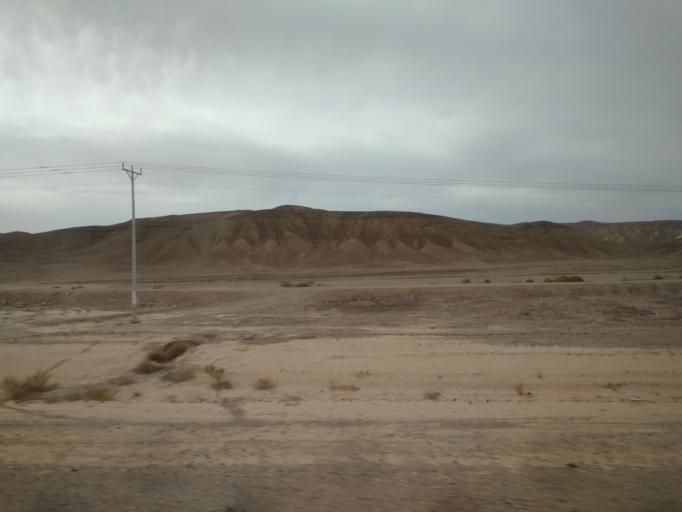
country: IL
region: Southern District
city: Eilat
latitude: 29.9561
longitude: 34.9231
